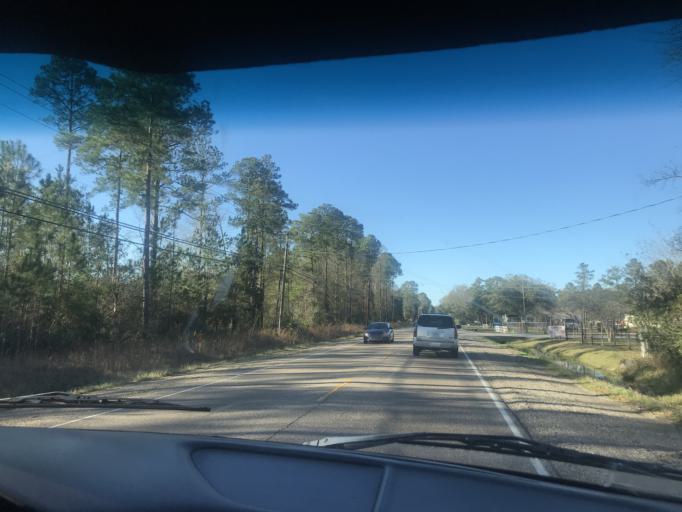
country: US
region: Louisiana
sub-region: Saint Tammany Parish
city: Covington
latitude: 30.5167
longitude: -90.1193
